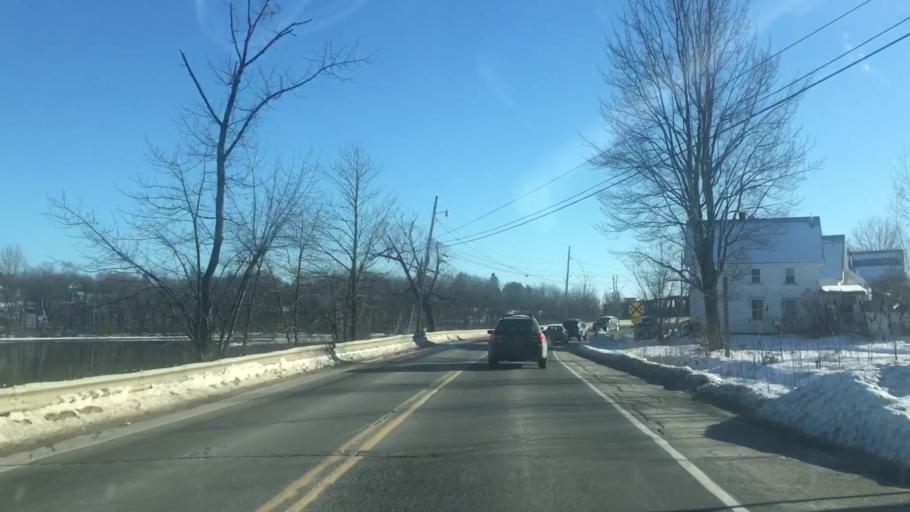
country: US
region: Maine
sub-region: Somerset County
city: Madison
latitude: 44.8032
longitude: -69.8880
